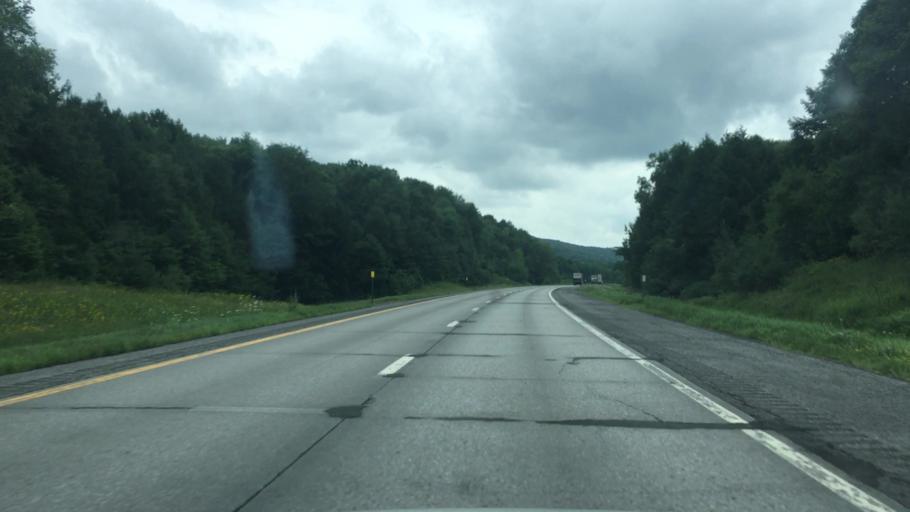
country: US
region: New York
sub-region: Otsego County
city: Worcester
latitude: 42.5971
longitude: -74.7106
